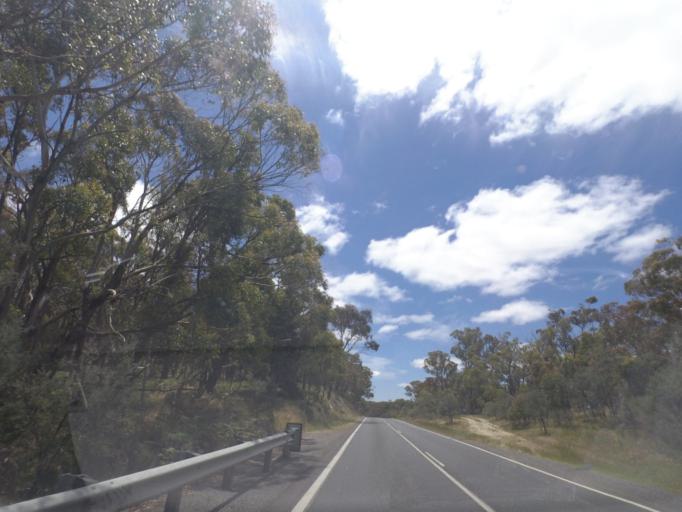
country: AU
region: Victoria
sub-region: Mount Alexander
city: Castlemaine
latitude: -37.2929
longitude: 144.1630
